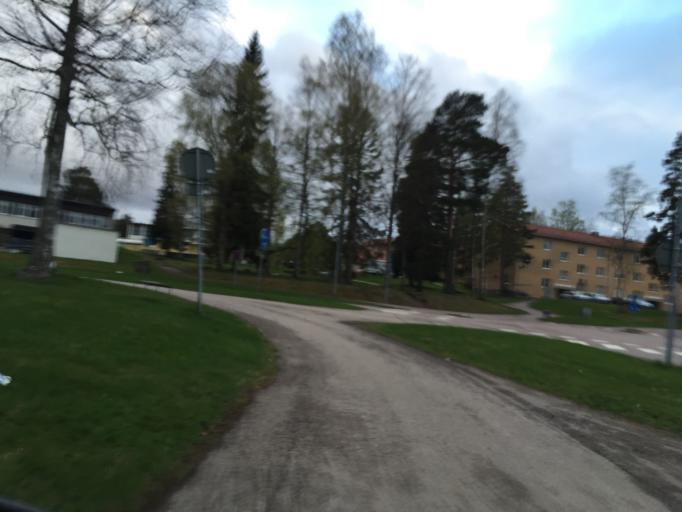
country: SE
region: Dalarna
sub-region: Ludvika Kommun
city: Ludvika
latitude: 60.1440
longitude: 15.1879
